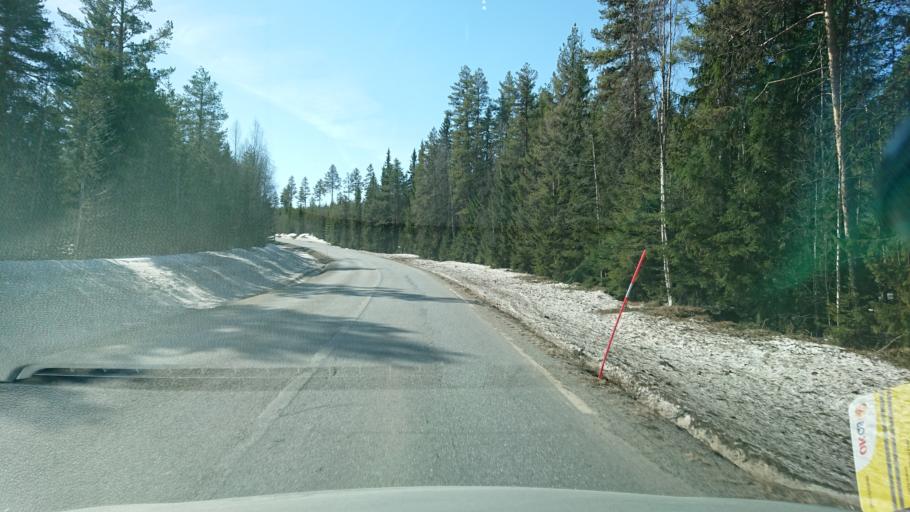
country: SE
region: Vaesterbotten
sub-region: Dorotea Kommun
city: Dorotea
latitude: 64.0754
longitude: 16.2549
